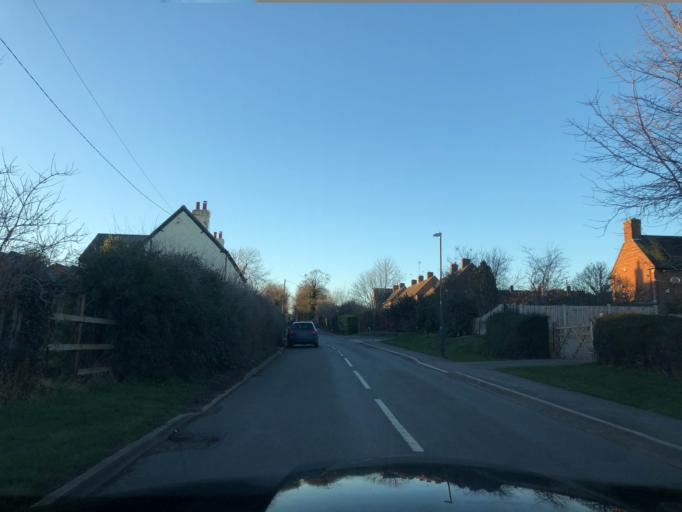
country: GB
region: England
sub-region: Warwickshire
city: Harbury
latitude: 52.2143
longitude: -1.4340
